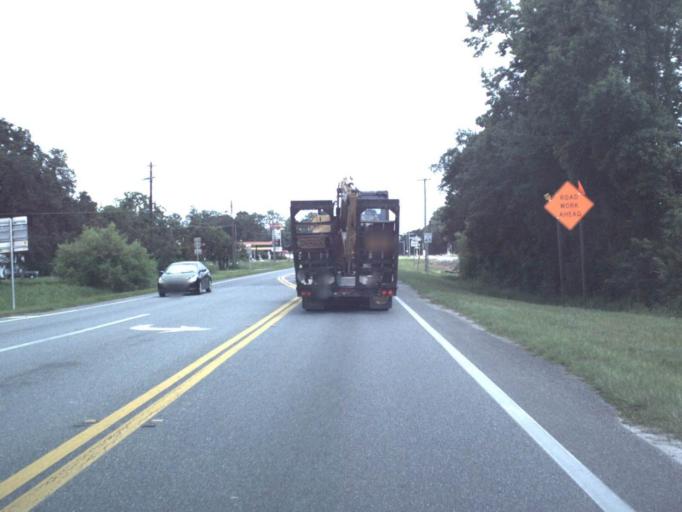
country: US
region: Florida
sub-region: Columbia County
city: Watertown
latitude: 30.1860
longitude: -82.6033
